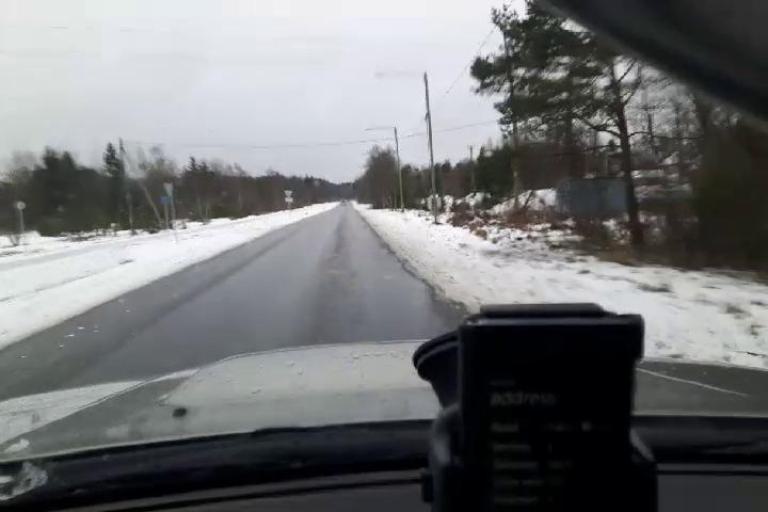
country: EE
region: Harju
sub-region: Harku vald
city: Tabasalu
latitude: 59.4345
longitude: 24.4957
